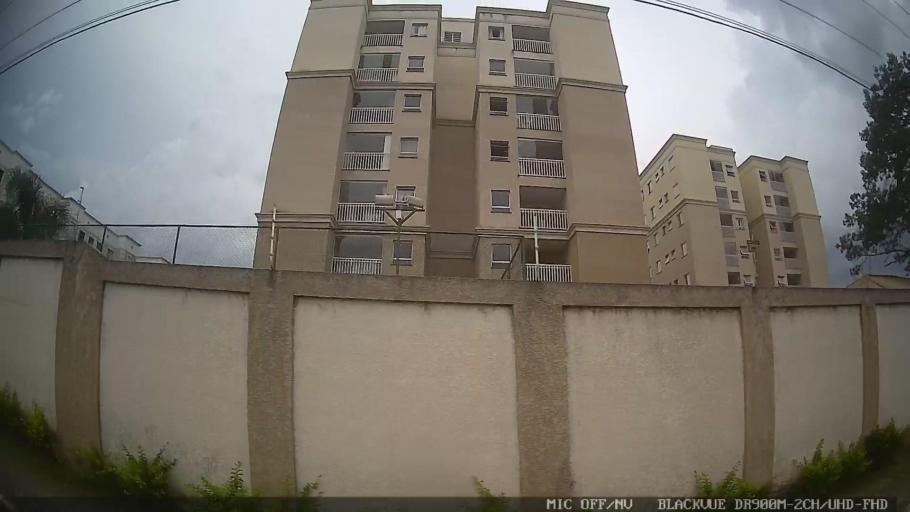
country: BR
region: Sao Paulo
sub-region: Suzano
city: Suzano
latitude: -23.5458
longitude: -46.2960
